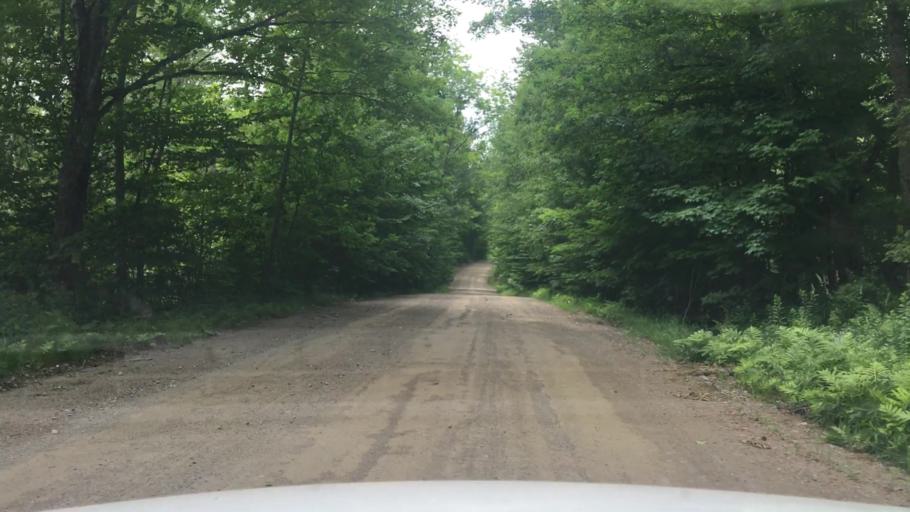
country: US
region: Maine
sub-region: Waldo County
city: Searsmont
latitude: 44.4167
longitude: -69.2630
